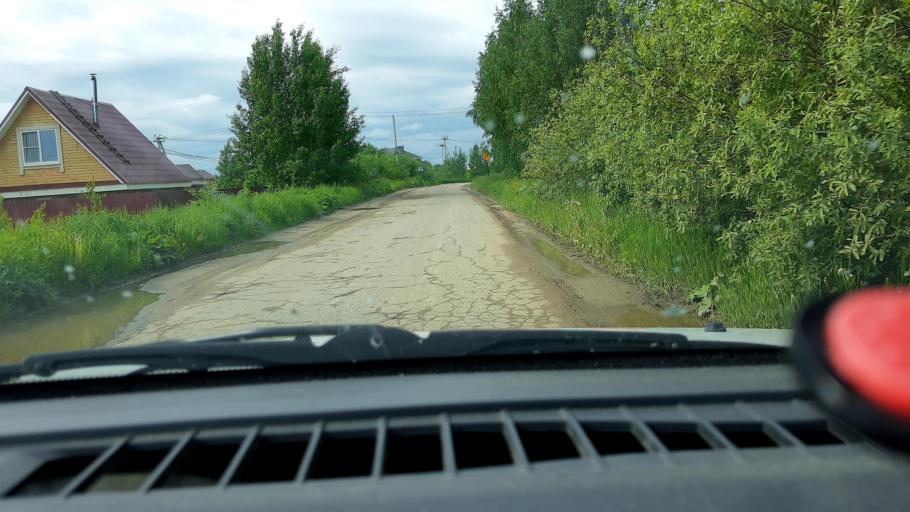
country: RU
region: Nizjnij Novgorod
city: Neklyudovo
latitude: 56.4258
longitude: 43.9635
